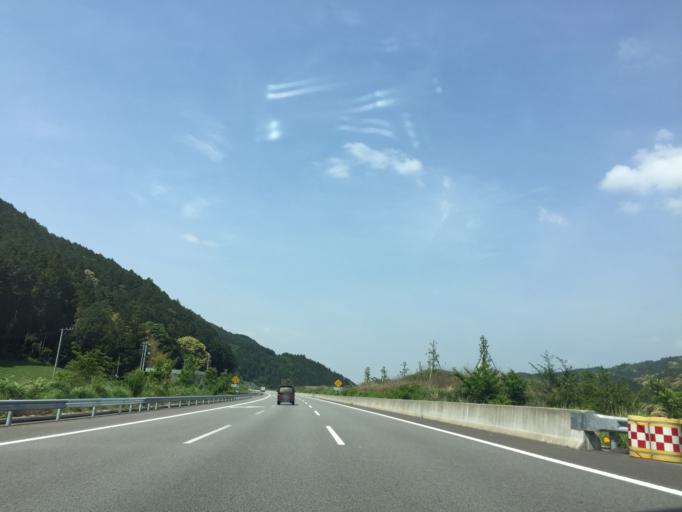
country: JP
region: Shizuoka
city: Mori
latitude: 34.8433
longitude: 137.9986
